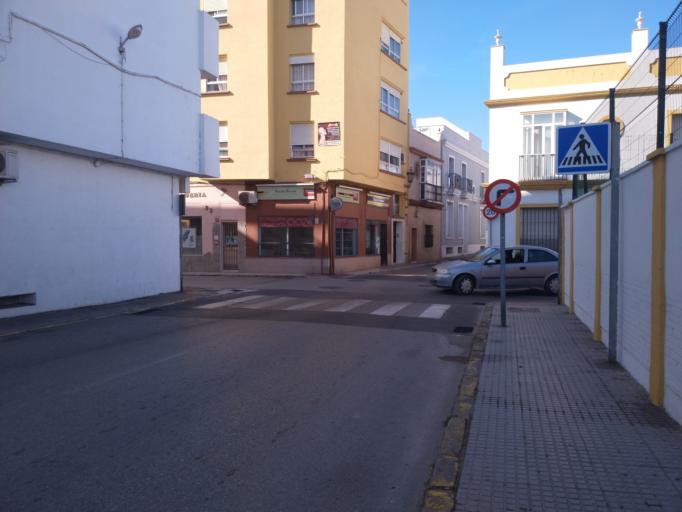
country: ES
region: Andalusia
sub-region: Provincia de Cadiz
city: San Fernando
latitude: 36.4689
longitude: -6.1910
